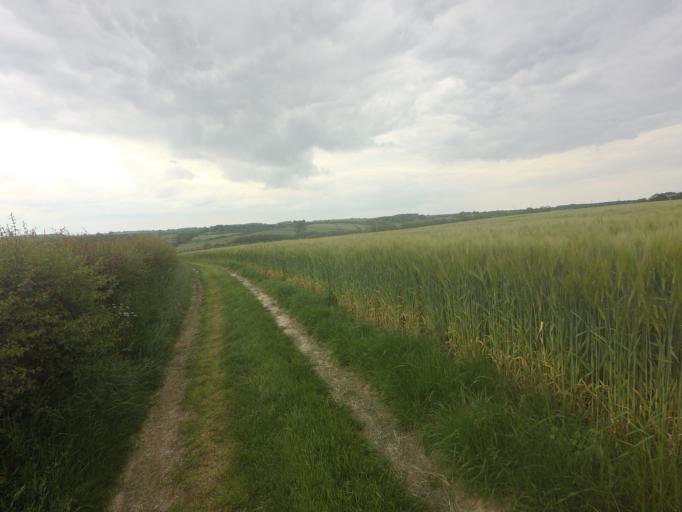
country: NL
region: Limburg
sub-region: Gemeente Voerendaal
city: Ubachsberg
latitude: 50.8040
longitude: 5.9412
